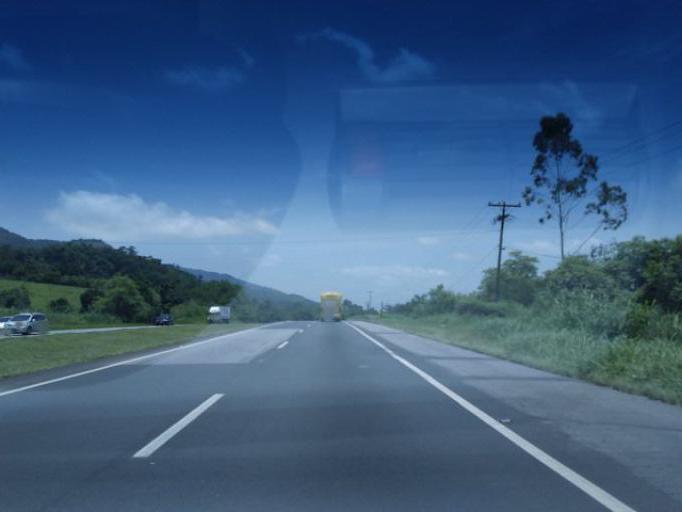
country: BR
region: Sao Paulo
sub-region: Miracatu
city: Miracatu
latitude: -24.2785
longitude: -47.4206
